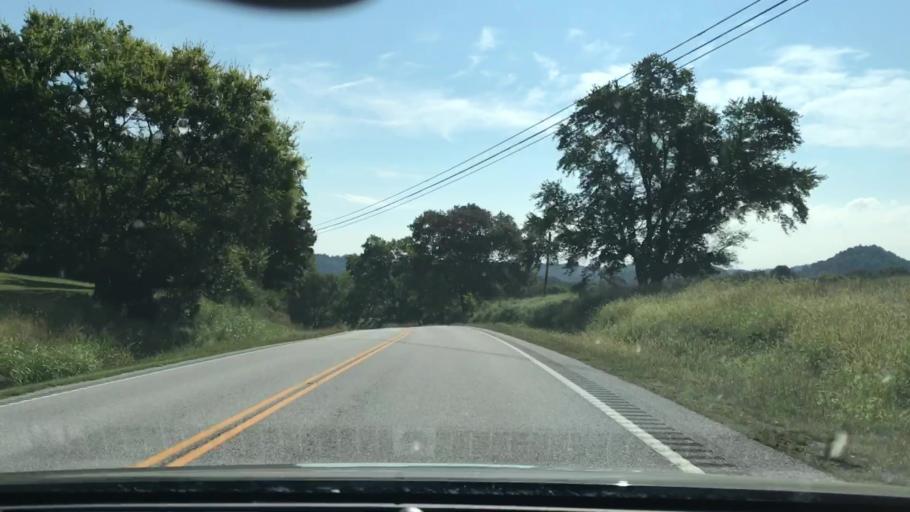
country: US
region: Tennessee
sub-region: Jackson County
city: Gainesboro
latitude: 36.3562
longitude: -85.7269
